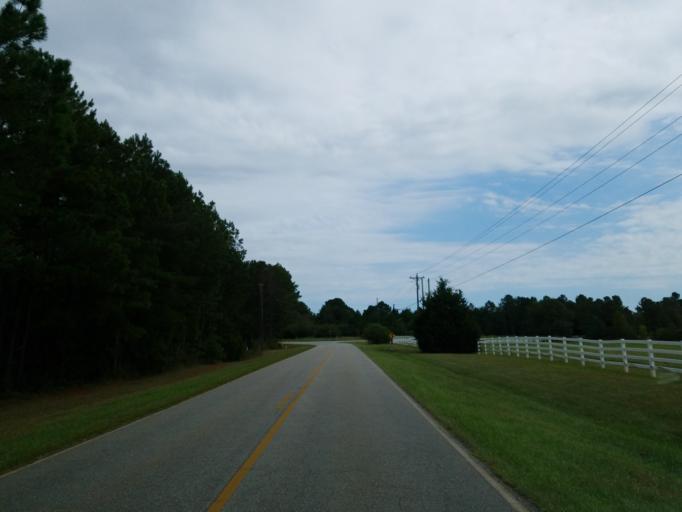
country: US
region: Georgia
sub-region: Monroe County
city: Forsyth
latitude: 32.9216
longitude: -83.9203
